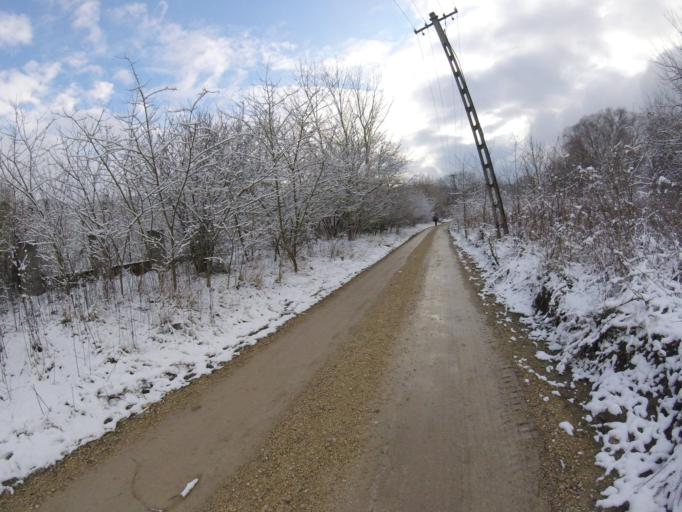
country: HU
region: Komarom-Esztergom
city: Esztergom
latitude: 47.7924
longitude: 18.7999
